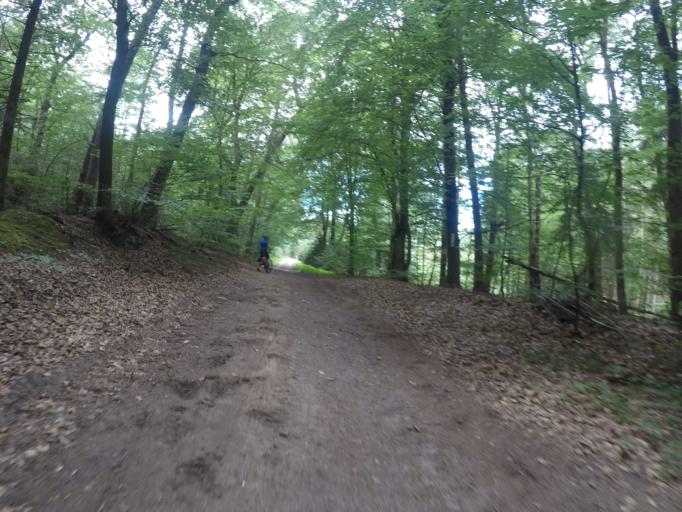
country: DE
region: Lower Saxony
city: Wingst
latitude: 53.7356
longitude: 9.0730
